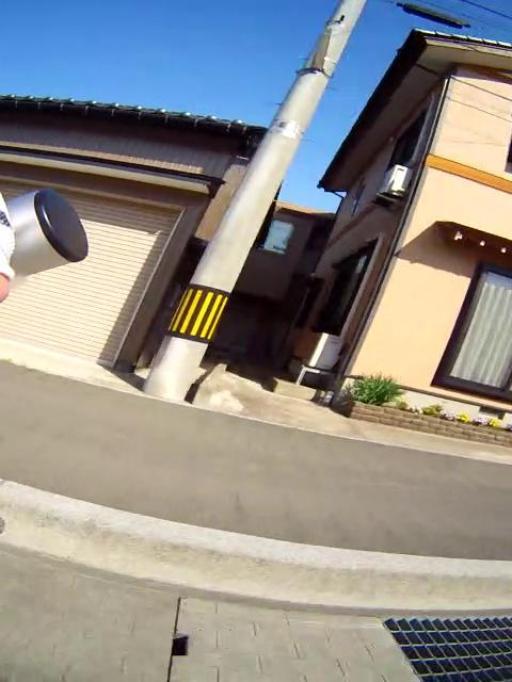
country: JP
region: Toyama
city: Fukumitsu
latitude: 36.5109
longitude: 136.9006
